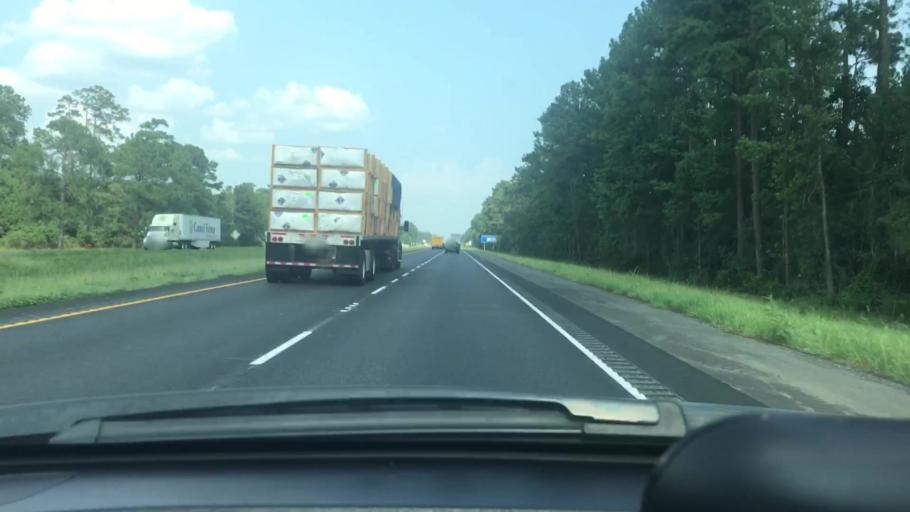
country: US
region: Louisiana
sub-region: Livingston Parish
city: Albany
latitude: 30.4745
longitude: -90.6626
